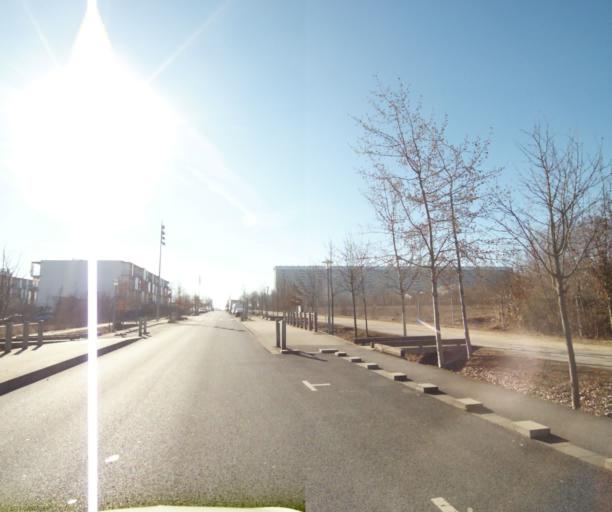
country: FR
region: Lorraine
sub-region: Departement de Meurthe-et-Moselle
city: Maxeville
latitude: 48.7043
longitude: 6.1502
